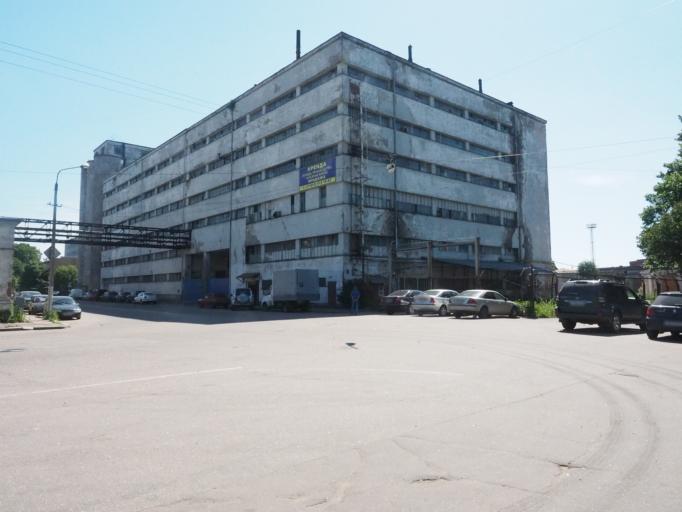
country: RU
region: Leningrad
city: Vyborg
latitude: 60.7072
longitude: 28.7383
